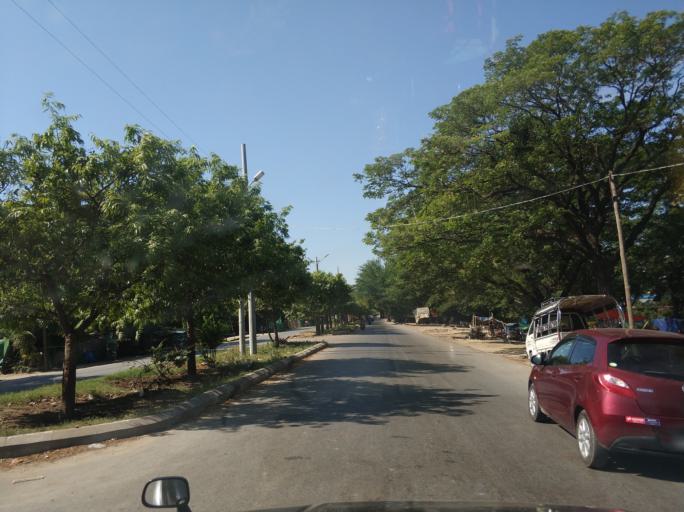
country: MM
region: Mandalay
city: Mandalay
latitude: 21.9653
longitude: 96.0560
